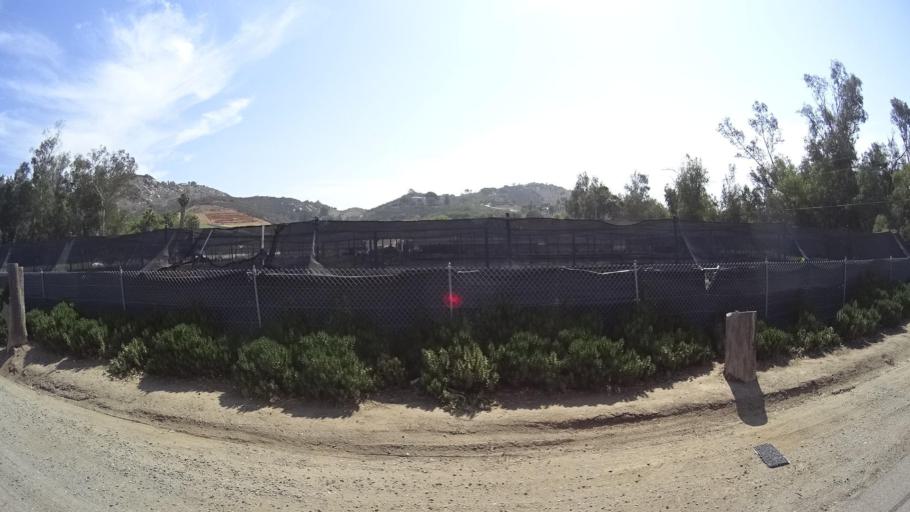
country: US
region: California
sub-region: San Diego County
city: San Marcos
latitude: 33.2018
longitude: -117.1673
